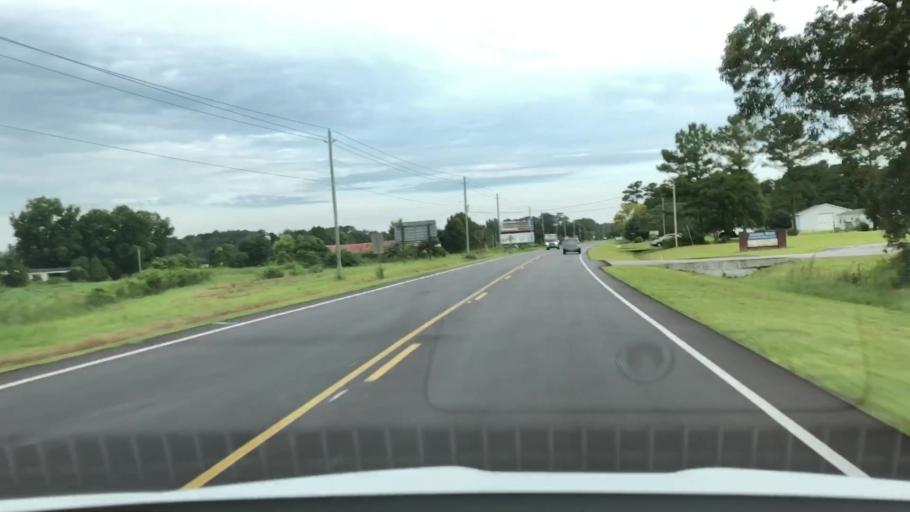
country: US
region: North Carolina
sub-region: Jones County
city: Maysville
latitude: 34.8615
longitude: -77.1891
